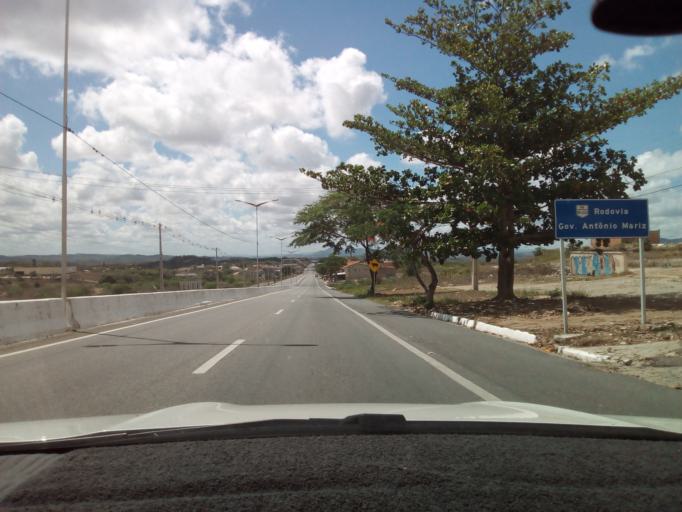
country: BR
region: Paraiba
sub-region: Campina Grande
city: Campina Grande
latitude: -7.2401
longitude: -35.8618
